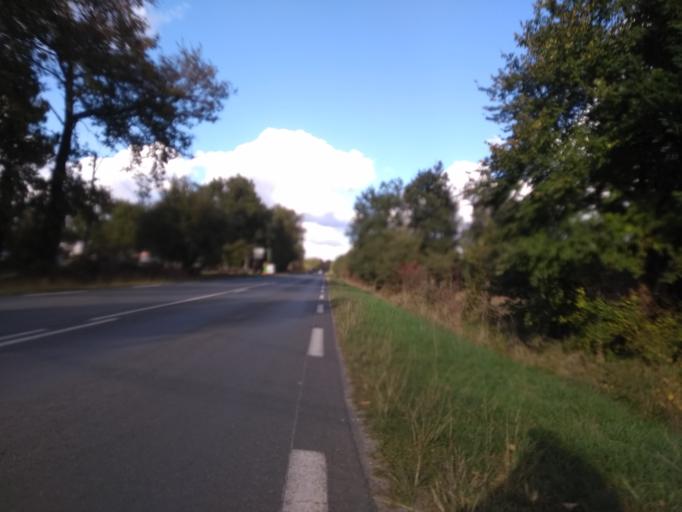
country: FR
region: Aquitaine
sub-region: Departement de la Gironde
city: Le Barp
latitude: 44.6732
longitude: -0.7296
